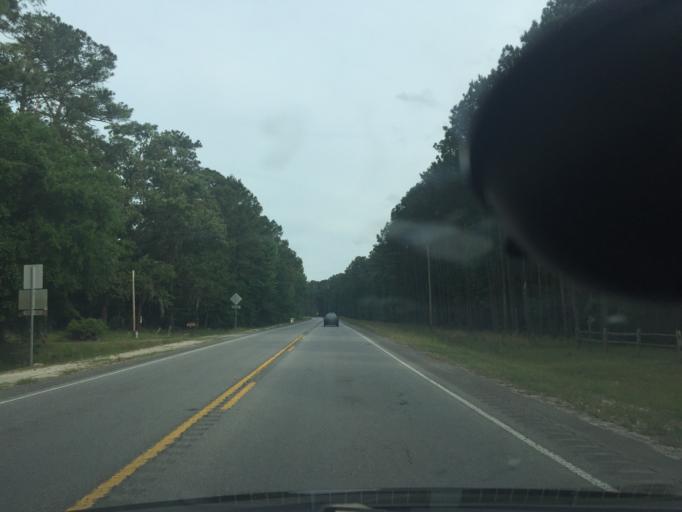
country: US
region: Georgia
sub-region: Bryan County
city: Richmond Hill
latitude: 32.0227
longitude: -81.3160
